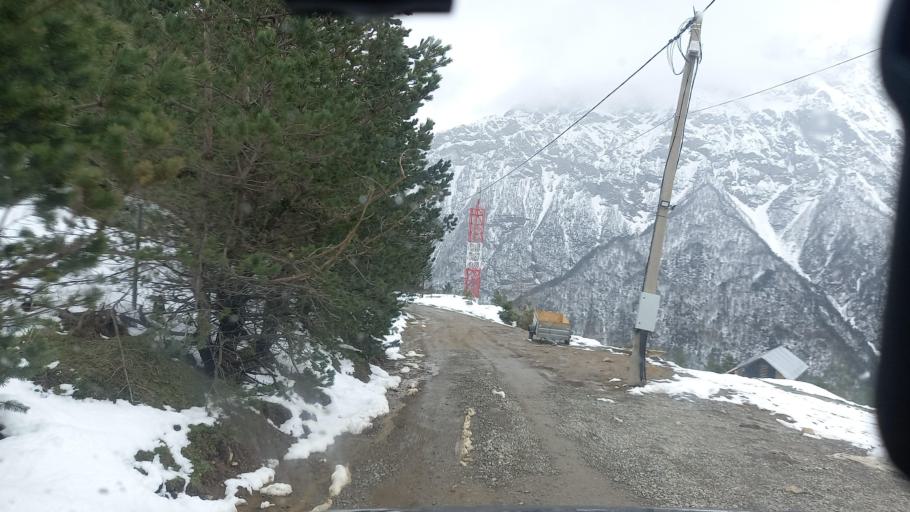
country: RU
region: North Ossetia
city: Mizur
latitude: 42.8097
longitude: 43.9568
